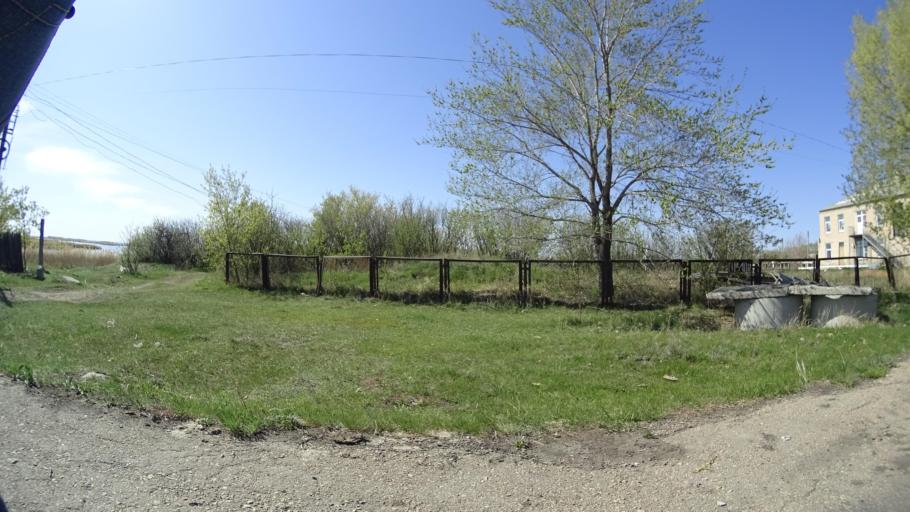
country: RU
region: Chelyabinsk
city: Chesma
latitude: 53.7951
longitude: 61.0296
